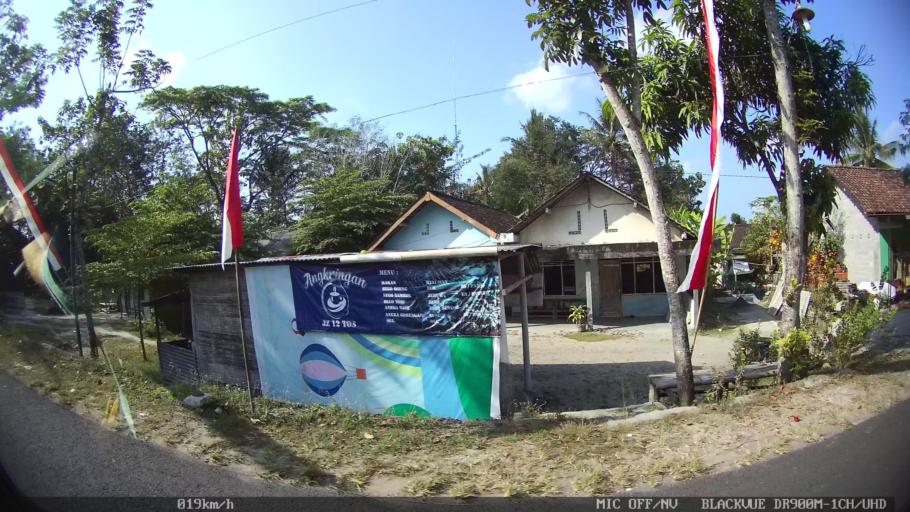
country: ID
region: Daerah Istimewa Yogyakarta
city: Kasihan
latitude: -7.8179
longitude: 110.2946
